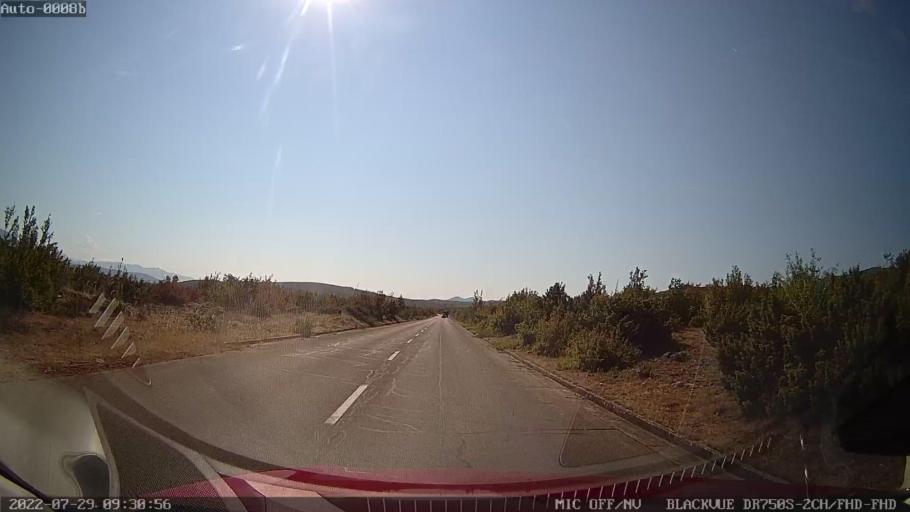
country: HR
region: Zadarska
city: Obrovac
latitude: 44.1920
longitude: 15.6925
